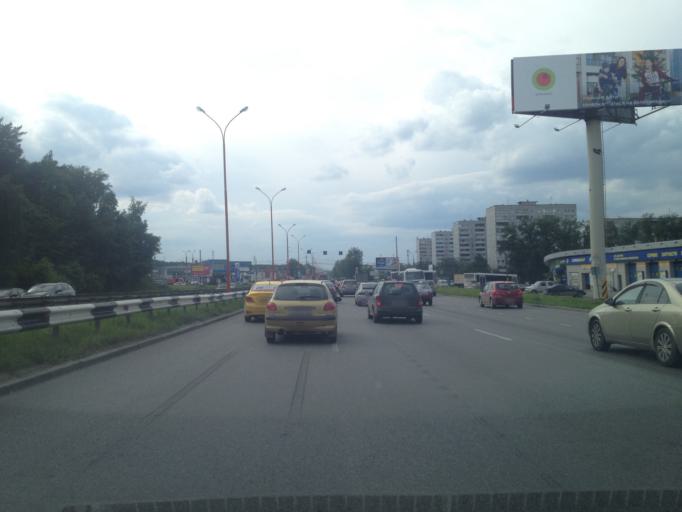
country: RU
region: Sverdlovsk
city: Sovkhoznyy
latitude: 56.7905
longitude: 60.5762
